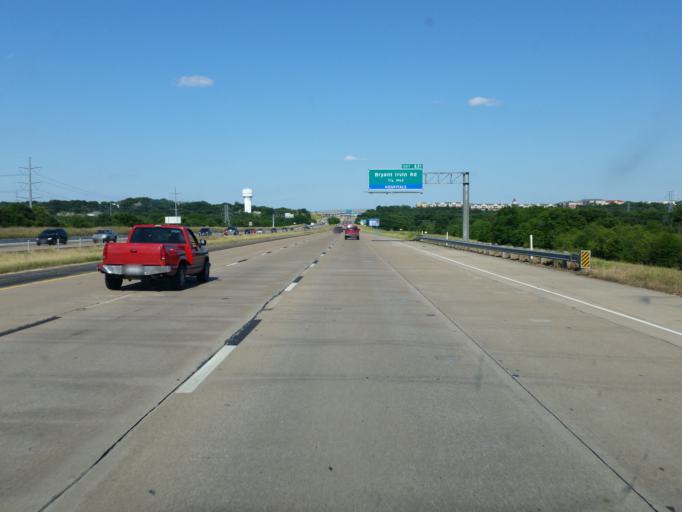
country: US
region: Texas
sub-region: Tarrant County
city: Benbrook
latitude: 32.6837
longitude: -97.4340
